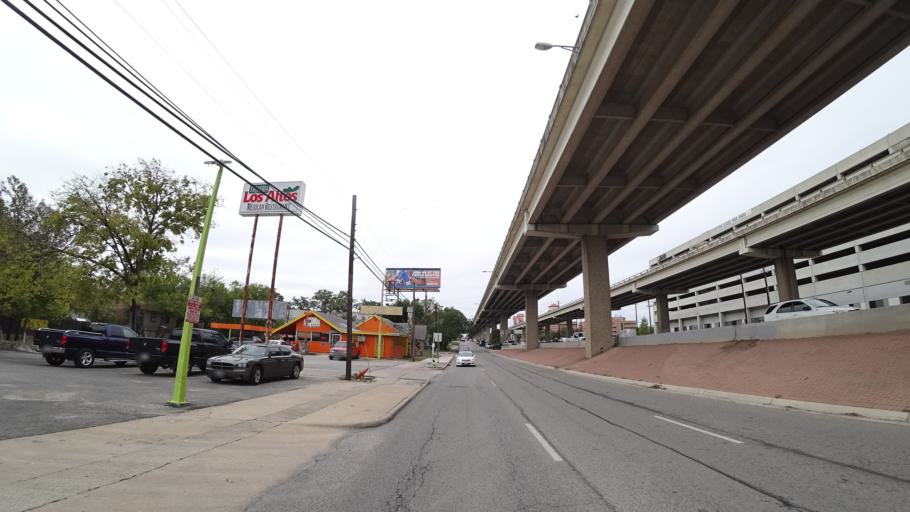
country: US
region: Texas
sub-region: Travis County
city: Austin
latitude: 30.2913
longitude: -97.7216
